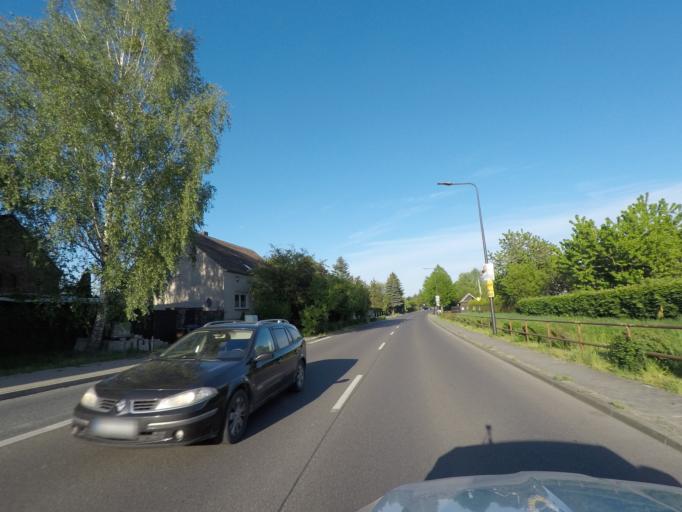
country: DE
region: Brandenburg
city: Hohenfinow
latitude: 52.8186
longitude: 13.8932
